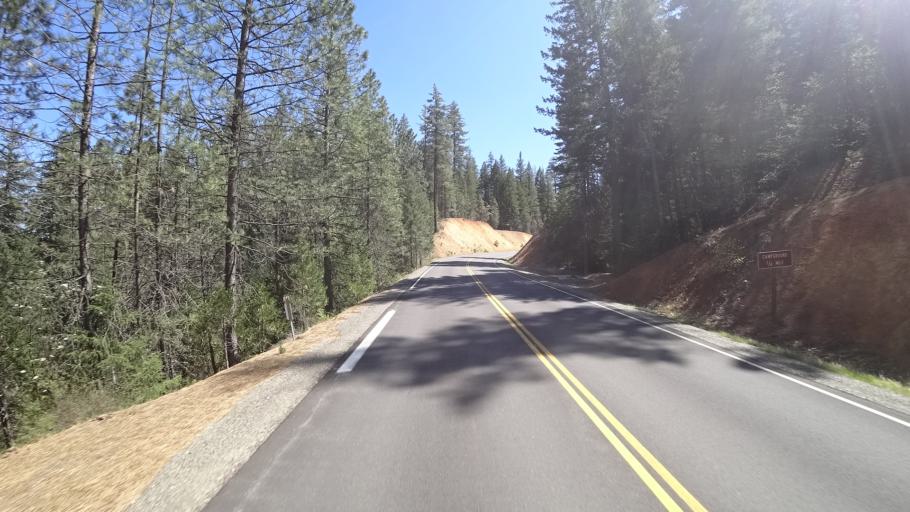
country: US
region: California
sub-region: Trinity County
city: Lewiston
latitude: 40.8899
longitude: -122.7951
